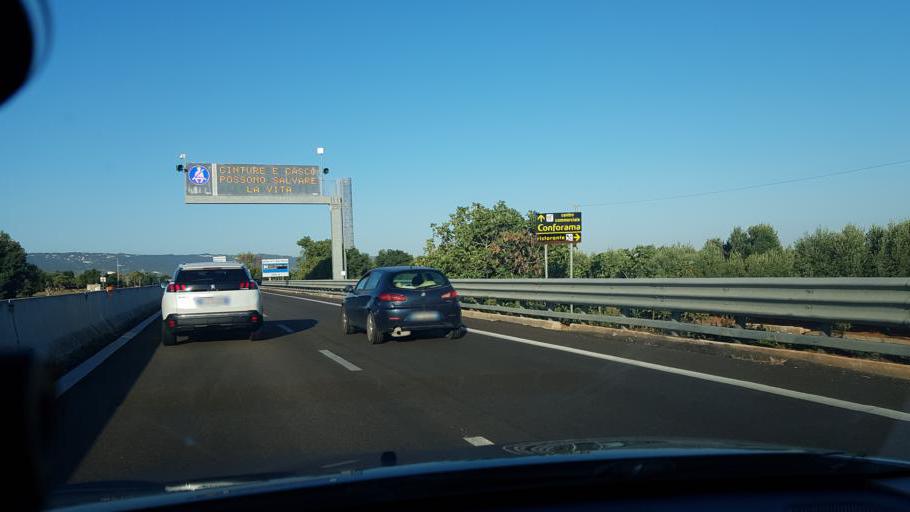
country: IT
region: Apulia
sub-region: Provincia di Brindisi
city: Pezze di Greco
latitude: 40.8337
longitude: 17.4110
